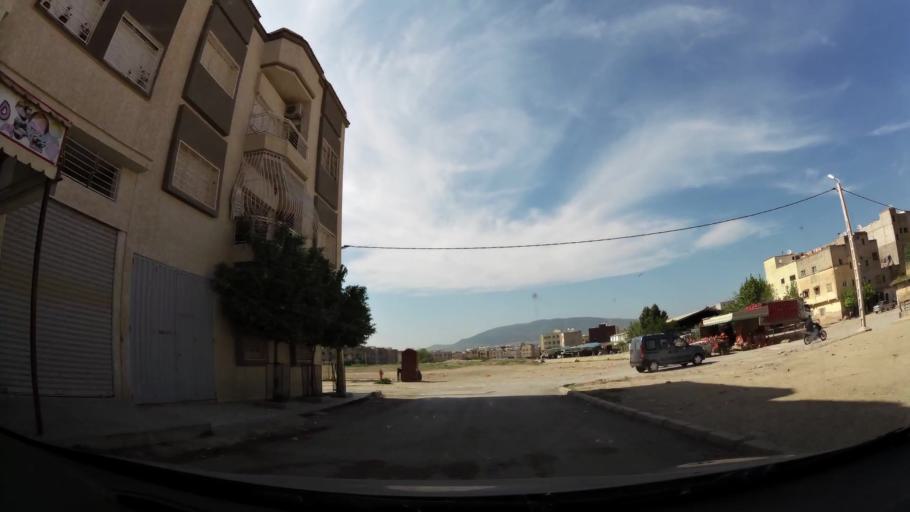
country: MA
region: Fes-Boulemane
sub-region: Fes
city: Fes
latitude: 34.0149
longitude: -5.0365
